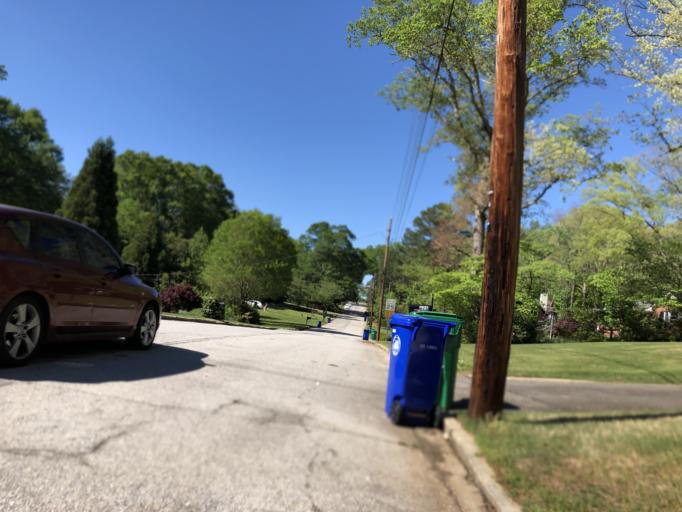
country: US
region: Georgia
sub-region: DeKalb County
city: North Decatur
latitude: 33.7960
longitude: -84.3001
